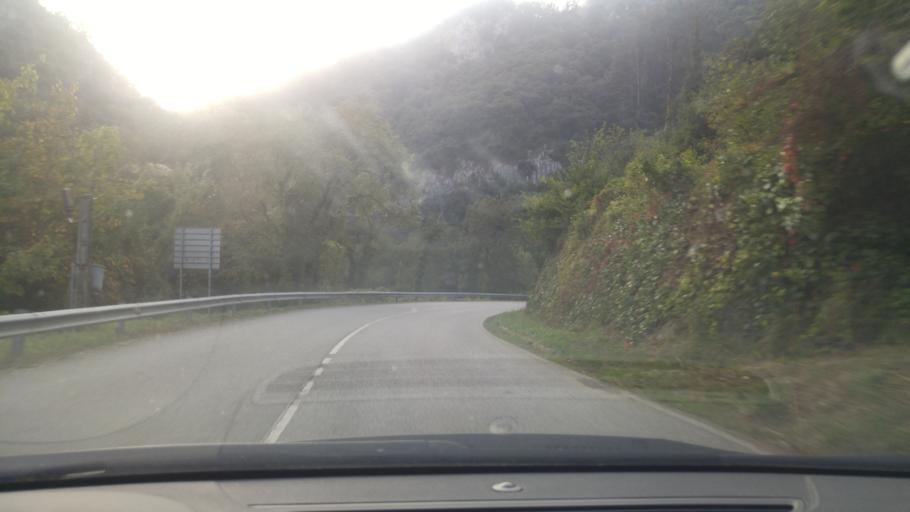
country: ES
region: Asturias
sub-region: Province of Asturias
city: Proaza
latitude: 43.2499
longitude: -6.0213
